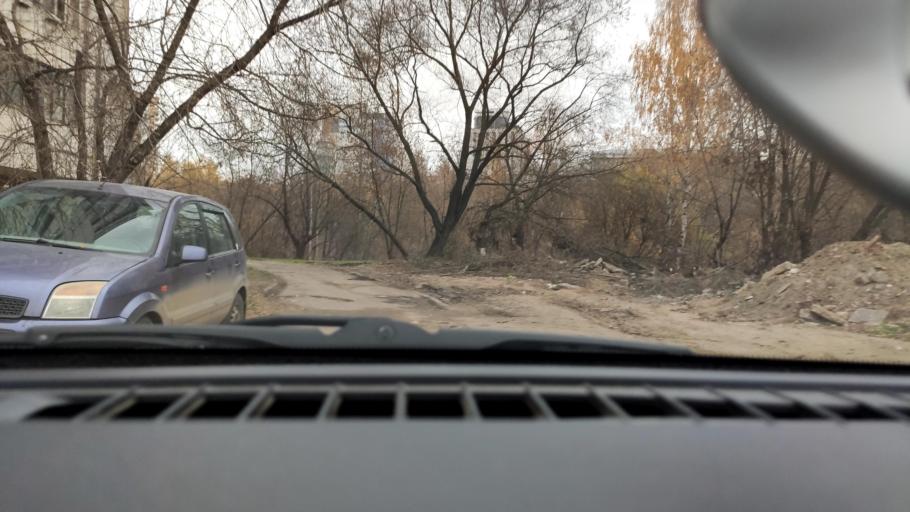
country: RU
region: Perm
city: Perm
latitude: 58.0036
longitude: 56.2799
